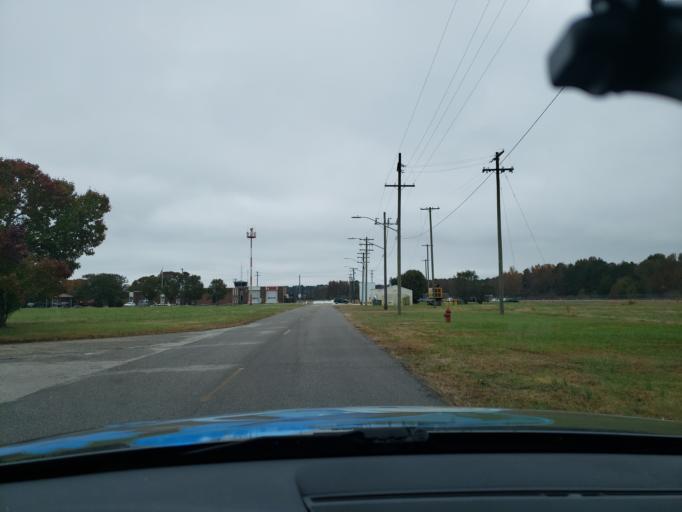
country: US
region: Virginia
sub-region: City of Chesapeake
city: Chesapeake
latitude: 36.7073
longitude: -76.1283
